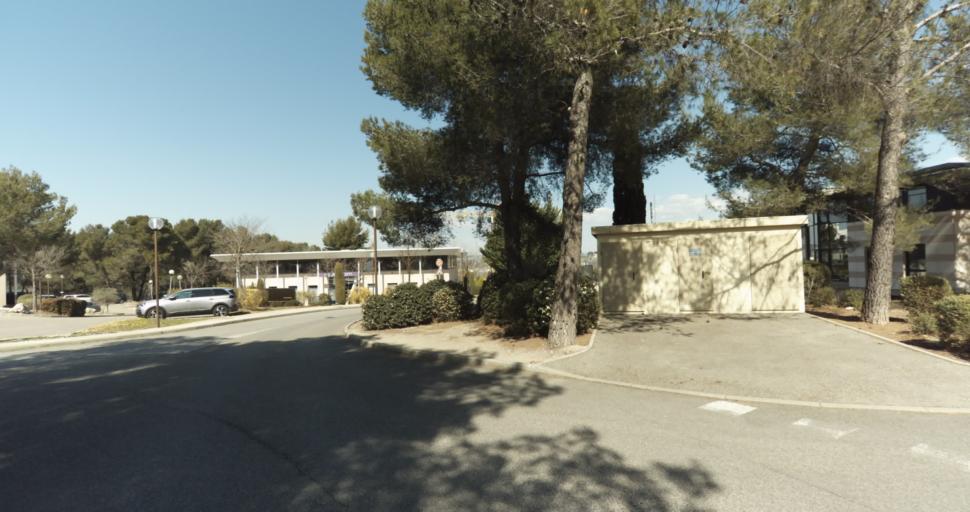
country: FR
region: Provence-Alpes-Cote d'Azur
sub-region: Departement des Bouches-du-Rhone
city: Cabries
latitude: 43.4781
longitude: 5.3702
